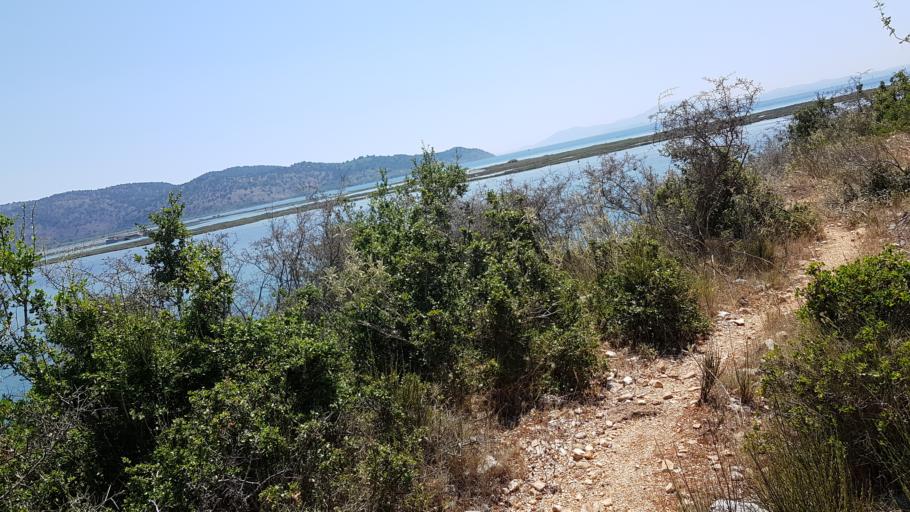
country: AL
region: Vlore
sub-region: Rrethi i Sarandes
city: Xarre
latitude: 39.7469
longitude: 19.9902
